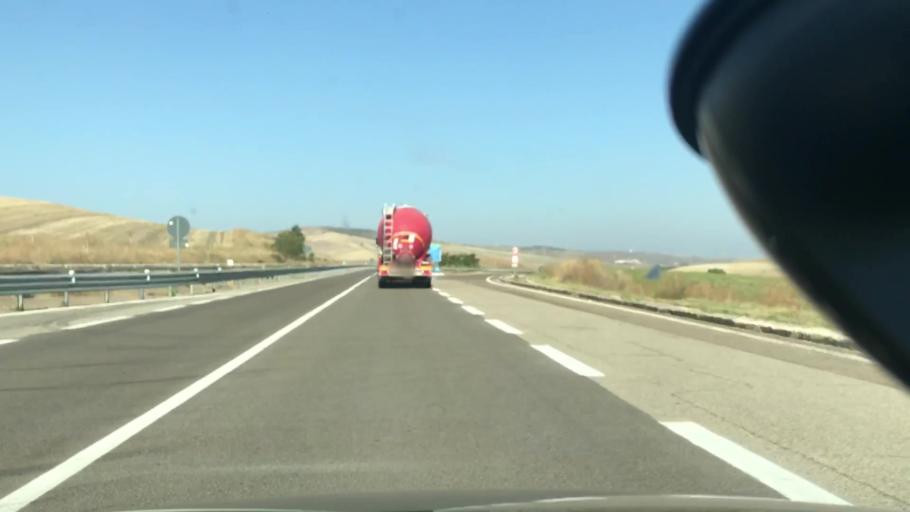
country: IT
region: Basilicate
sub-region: Provincia di Matera
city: Irsina
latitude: 40.7862
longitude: 16.2954
